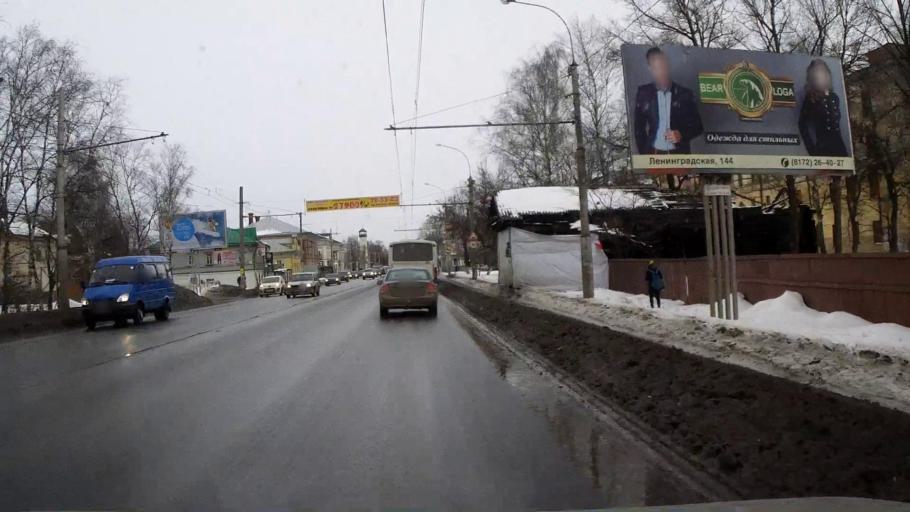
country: RU
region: Vologda
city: Vologda
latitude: 59.2255
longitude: 39.8928
